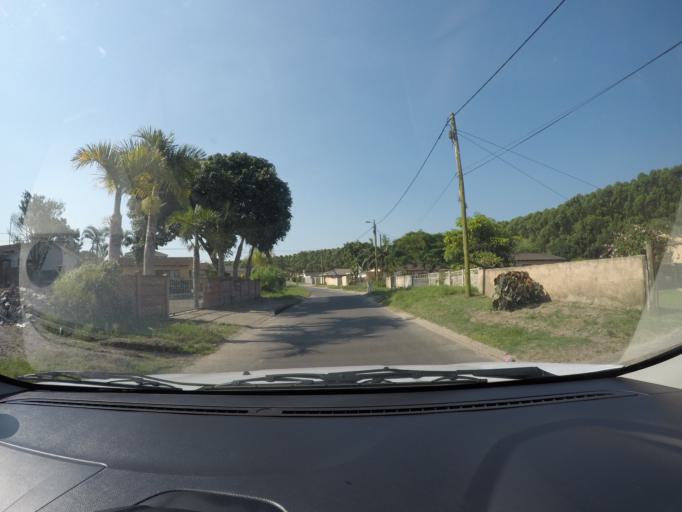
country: ZA
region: KwaZulu-Natal
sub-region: uThungulu District Municipality
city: Richards Bay
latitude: -28.7166
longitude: 32.0441
